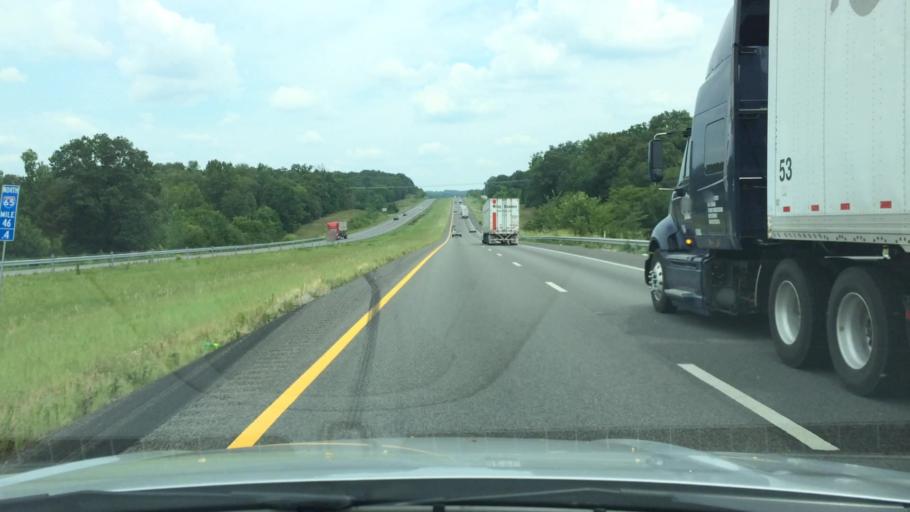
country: US
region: Tennessee
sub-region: Maury County
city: Spring Hill
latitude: 35.6473
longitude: -86.8933
